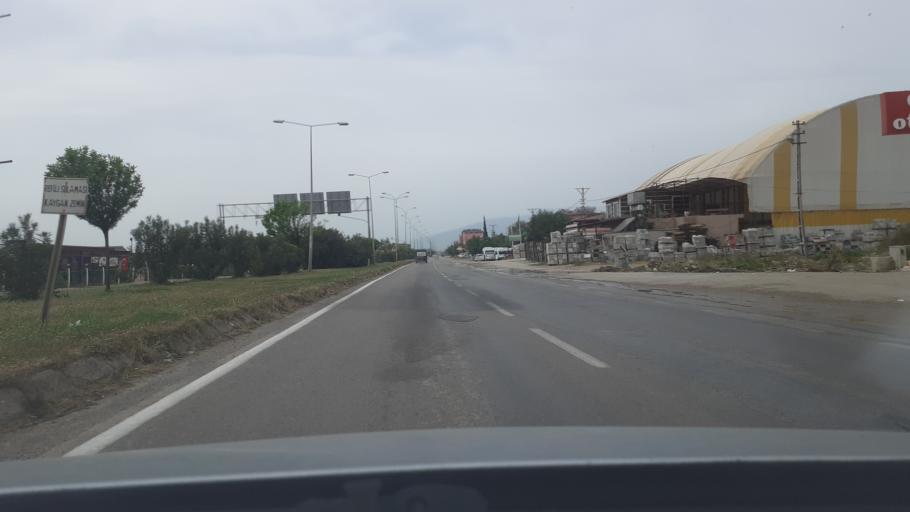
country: TR
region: Hatay
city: Kirikhan
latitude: 36.4868
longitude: 36.3653
